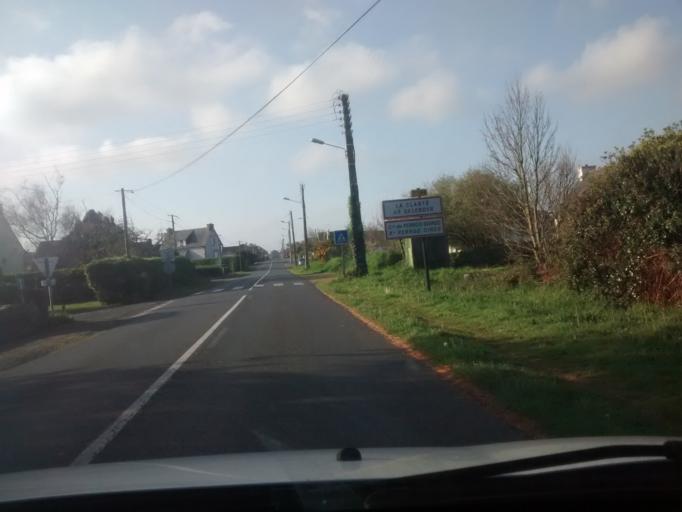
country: FR
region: Brittany
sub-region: Departement des Cotes-d'Armor
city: Tregastel
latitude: 48.8235
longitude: -3.4716
